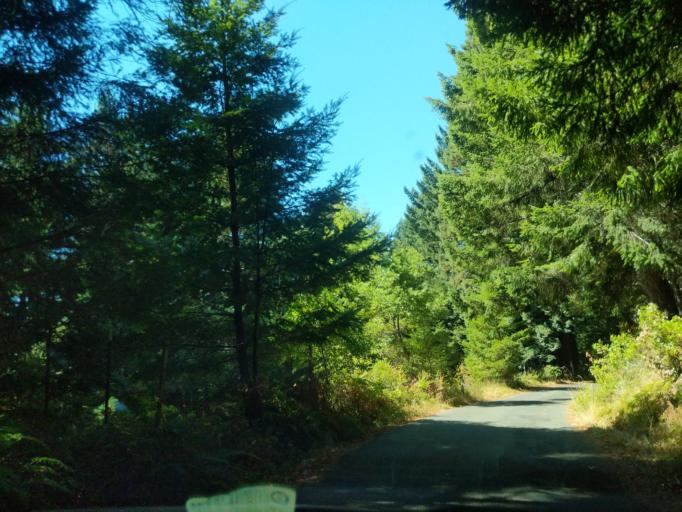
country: US
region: California
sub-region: Sonoma County
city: Monte Rio
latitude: 38.5239
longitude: -123.2349
